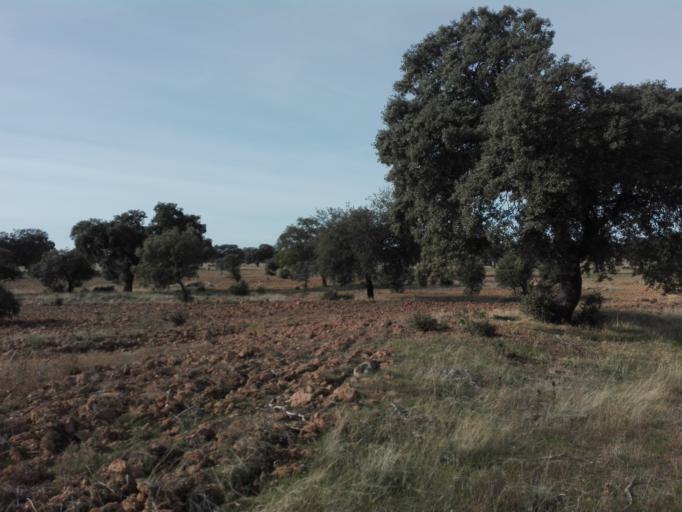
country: ES
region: Extremadura
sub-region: Provincia de Badajoz
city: Campillo de Llerena
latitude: 38.4589
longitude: -5.8755
